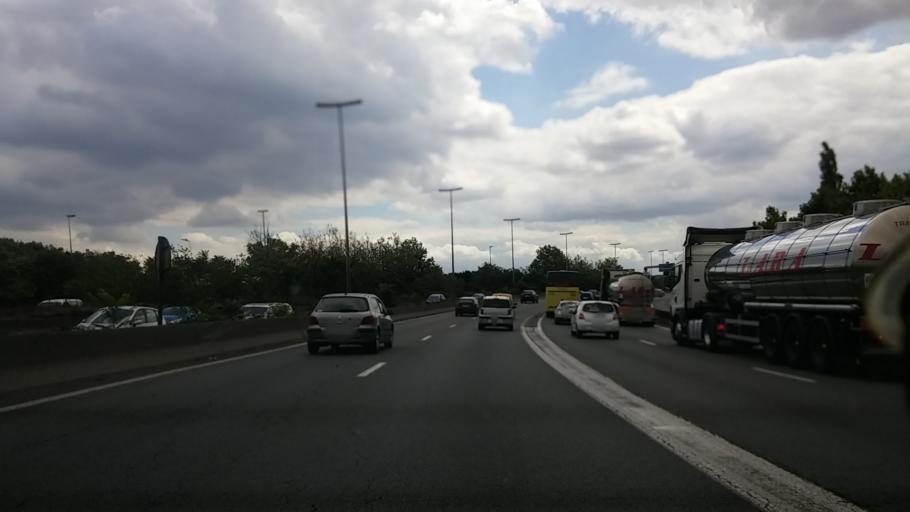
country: FR
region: Ile-de-France
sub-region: Departement de Seine-Saint-Denis
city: Noisy-le-Sec
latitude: 48.8889
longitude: 2.4739
